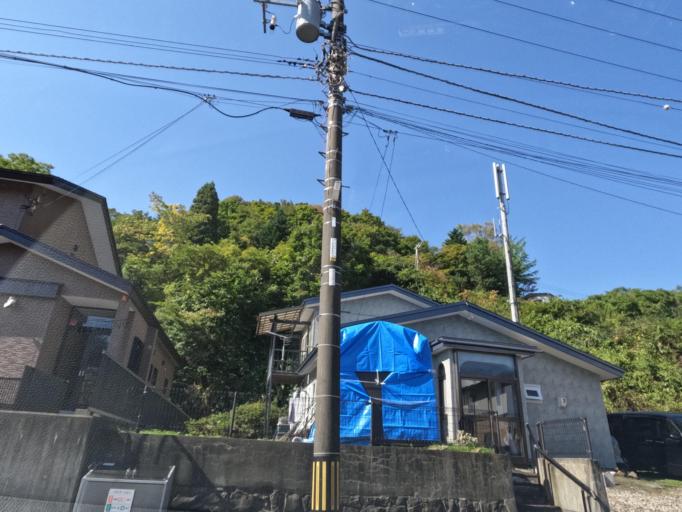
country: JP
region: Hokkaido
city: Muroran
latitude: 42.3691
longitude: 141.0256
